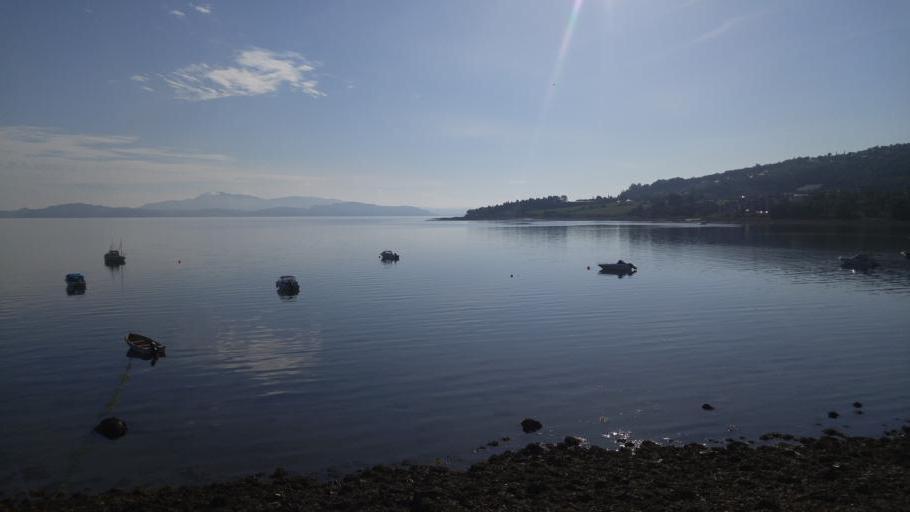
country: NO
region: Sor-Trondelag
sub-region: Malvik
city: Malvik
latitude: 63.4397
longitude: 10.6086
